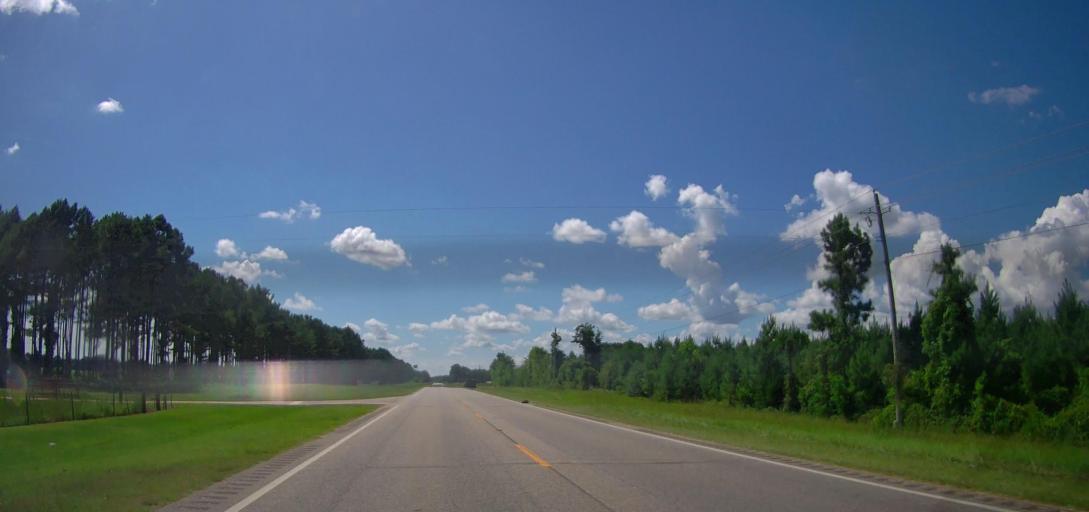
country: US
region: Alabama
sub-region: Elmore County
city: Tallassee
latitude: 32.3891
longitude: -85.8916
